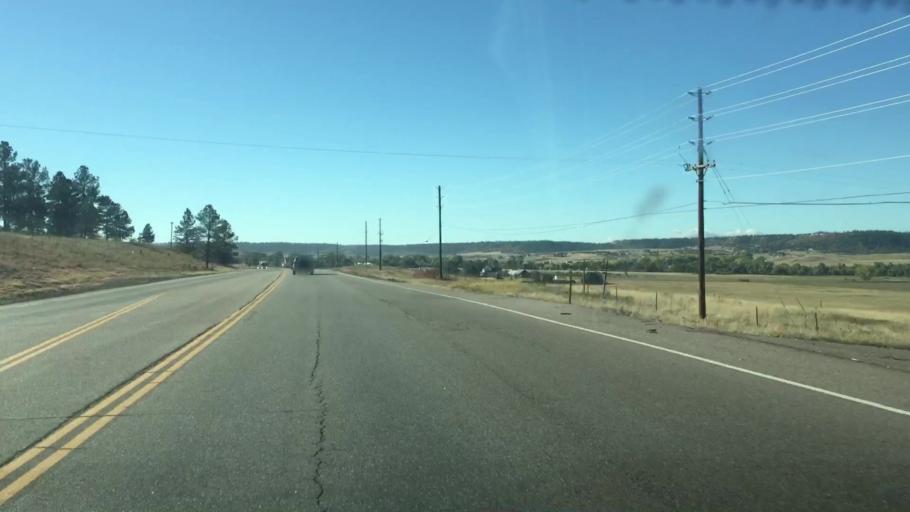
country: US
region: Colorado
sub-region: Douglas County
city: The Pinery
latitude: 39.4147
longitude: -104.7608
